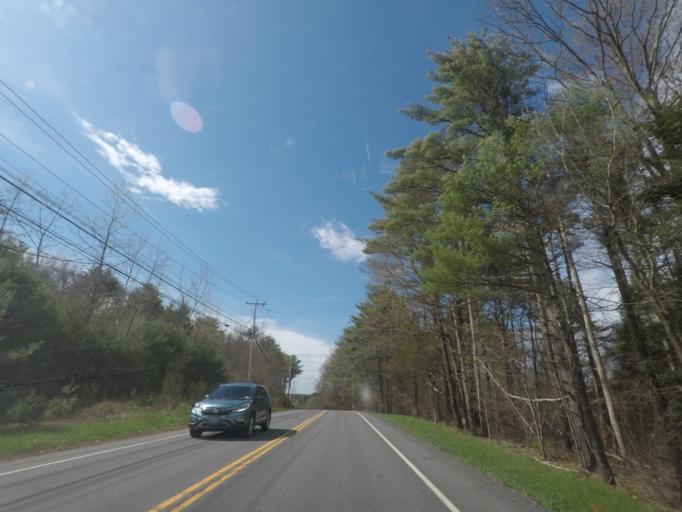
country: US
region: New York
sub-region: Greene County
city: Cairo
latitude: 42.3119
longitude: -74.0077
